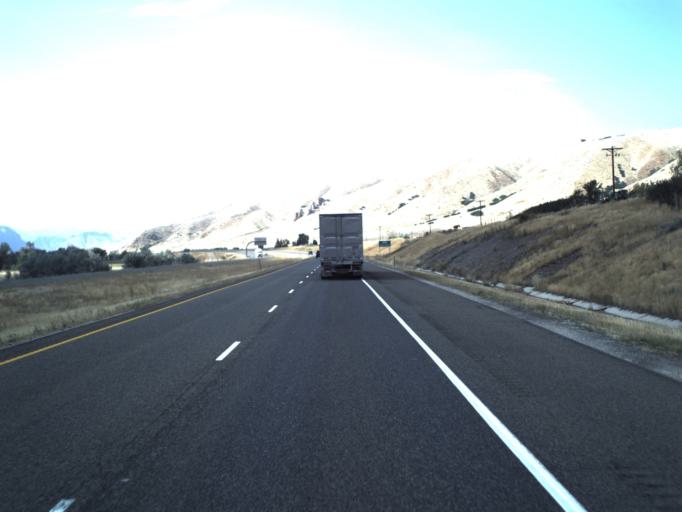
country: US
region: Utah
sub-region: Summit County
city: Coalville
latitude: 40.9794
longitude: -111.4466
